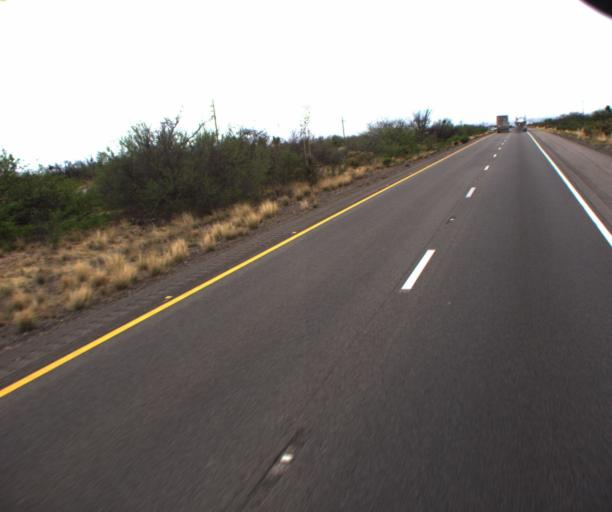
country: US
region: Arizona
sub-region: Cochise County
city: Saint David
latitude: 32.0052
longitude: -110.1424
